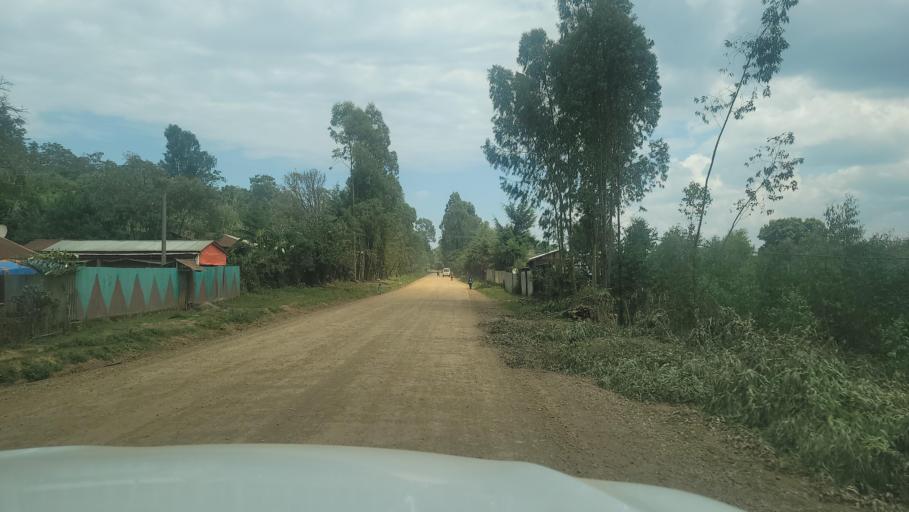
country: ET
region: Oromiya
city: Agaro
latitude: 7.7514
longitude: 36.2646
